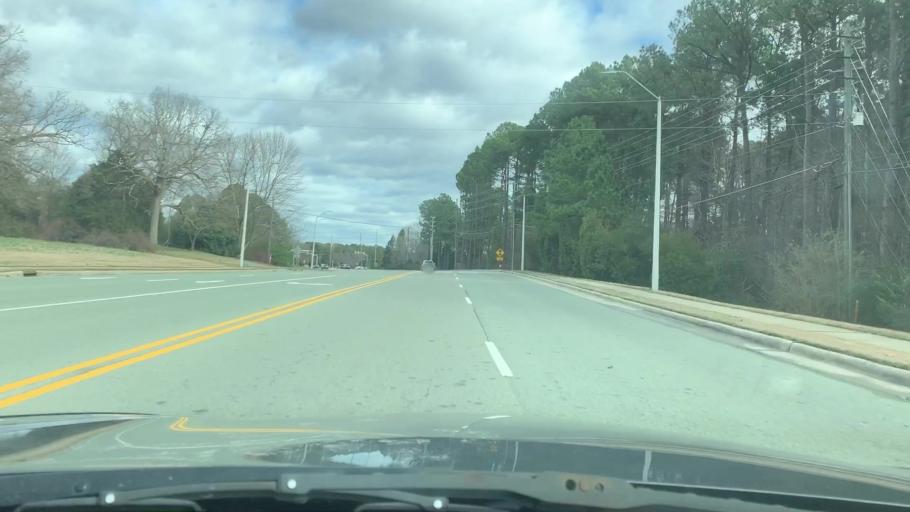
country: US
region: North Carolina
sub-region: Wake County
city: Cary
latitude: 35.8169
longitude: -78.7732
